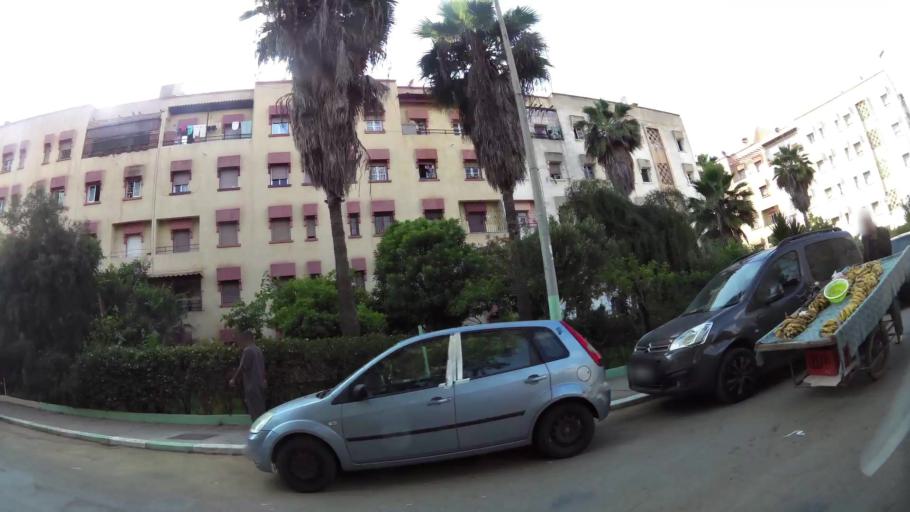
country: MA
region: Rabat-Sale-Zemmour-Zaer
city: Sale
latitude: 34.0472
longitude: -6.8073
